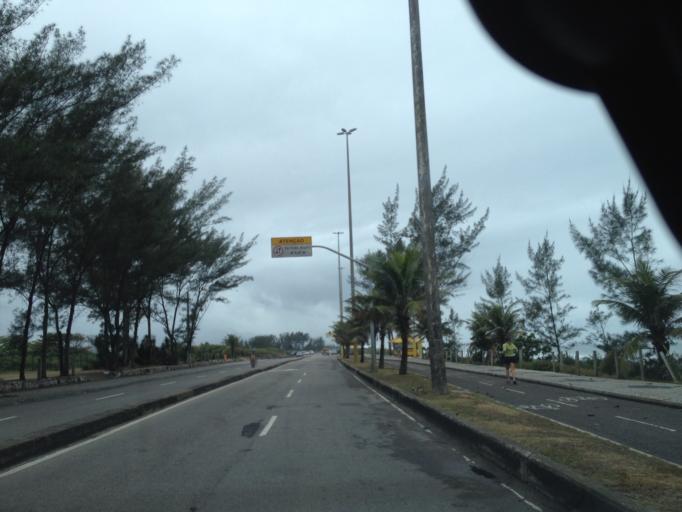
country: BR
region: Rio de Janeiro
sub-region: Nilopolis
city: Nilopolis
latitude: -23.0211
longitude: -43.4417
